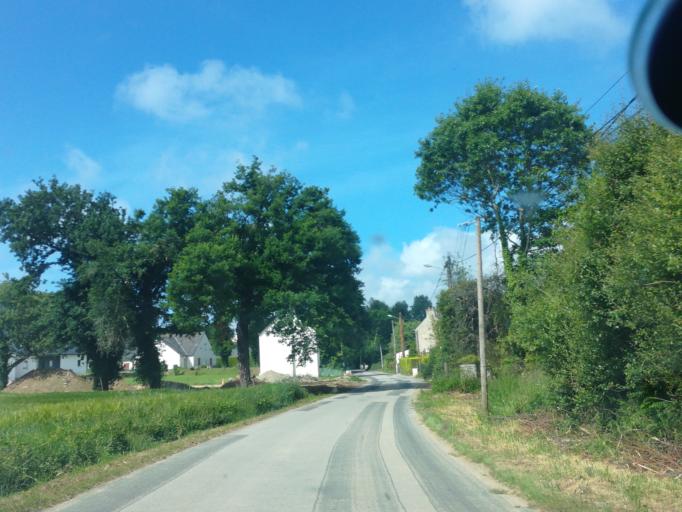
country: FR
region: Brittany
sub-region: Departement du Morbihan
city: Pontivy
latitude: 48.0735
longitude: -2.9483
